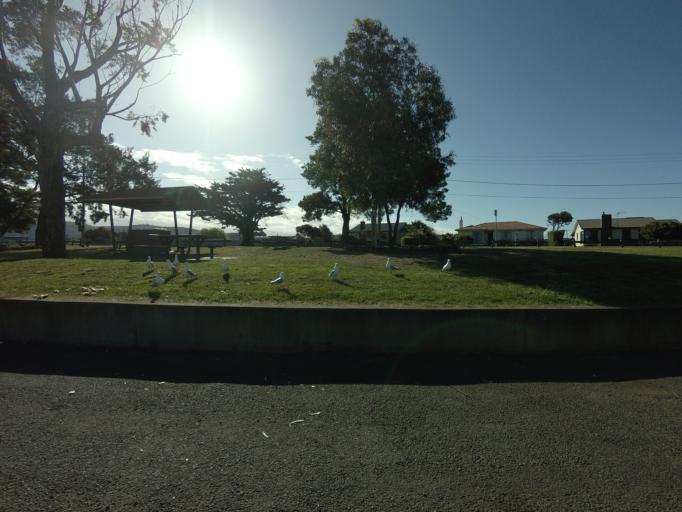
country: AU
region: Tasmania
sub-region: Sorell
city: Sorell
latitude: -42.5093
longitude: 147.9161
